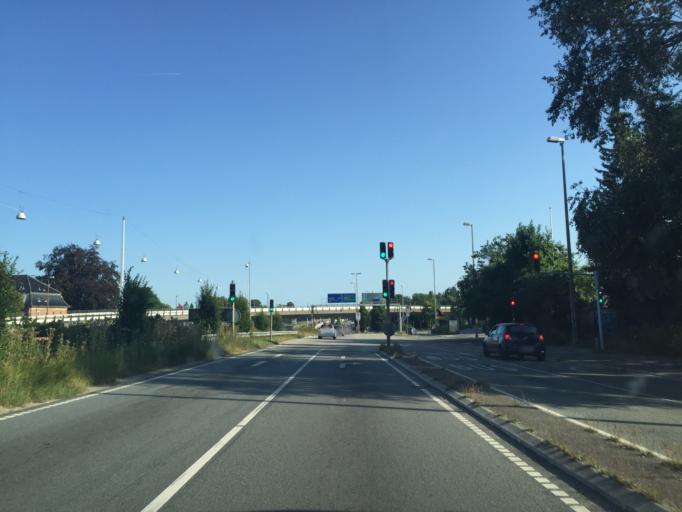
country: DK
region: Capital Region
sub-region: Gentofte Kommune
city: Charlottenlund
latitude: 55.7284
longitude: 12.5492
